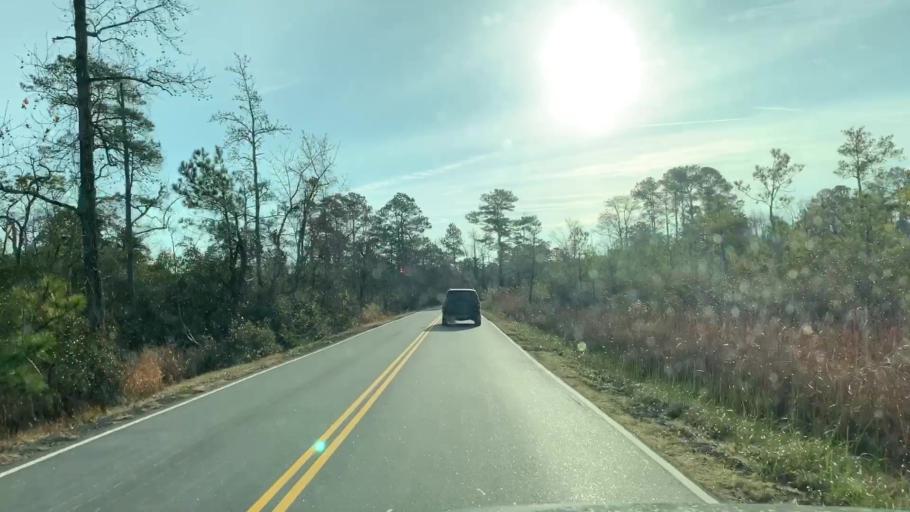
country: US
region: Virginia
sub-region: City of Virginia Beach
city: Virginia Beach
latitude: 36.6943
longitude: -76.0388
